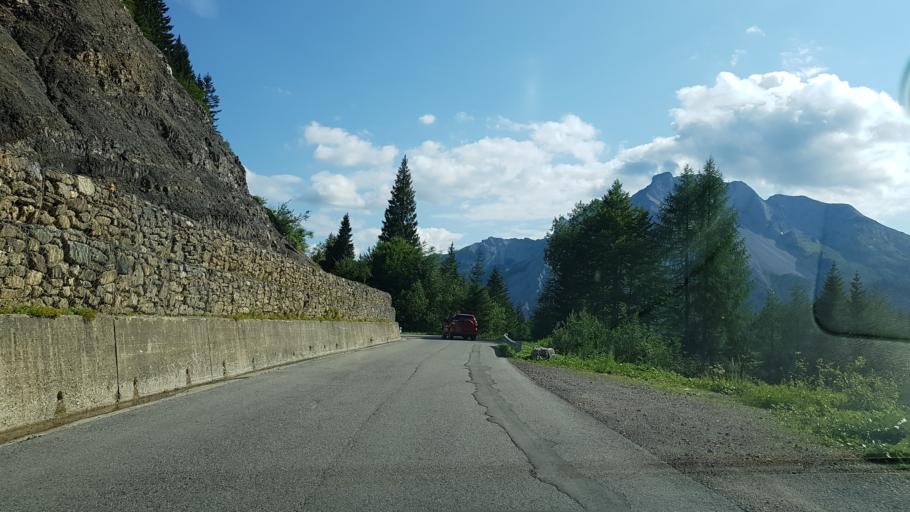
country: IT
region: Friuli Venezia Giulia
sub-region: Provincia di Udine
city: Sauris di Sotto
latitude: 46.4771
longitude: 12.6600
